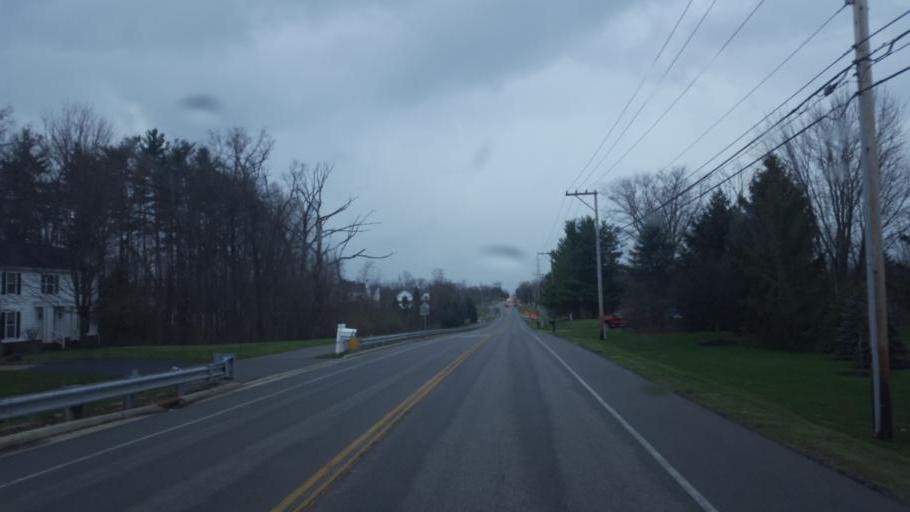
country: US
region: Ohio
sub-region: Delaware County
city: Lewis Center
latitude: 40.1738
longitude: -82.9867
